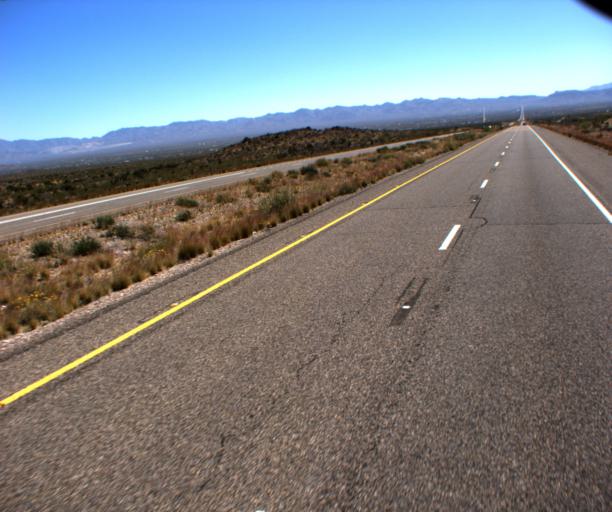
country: US
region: Arizona
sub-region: Mohave County
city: Golden Valley
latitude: 35.2288
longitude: -114.3590
